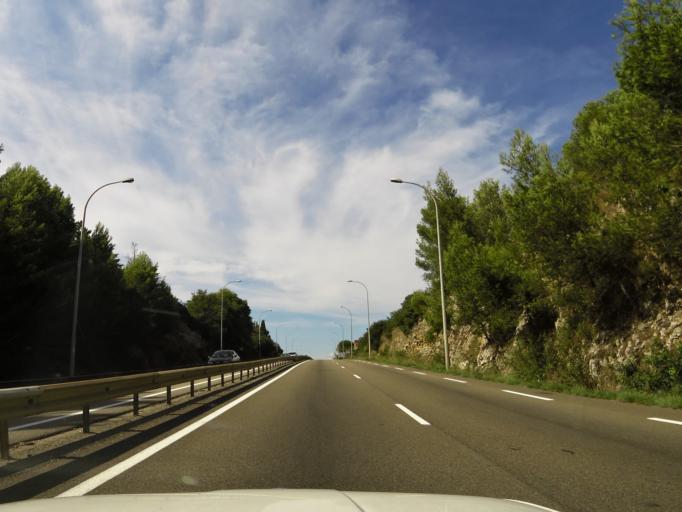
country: FR
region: Languedoc-Roussillon
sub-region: Departement du Gard
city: Nimes
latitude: 43.8356
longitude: 4.3215
